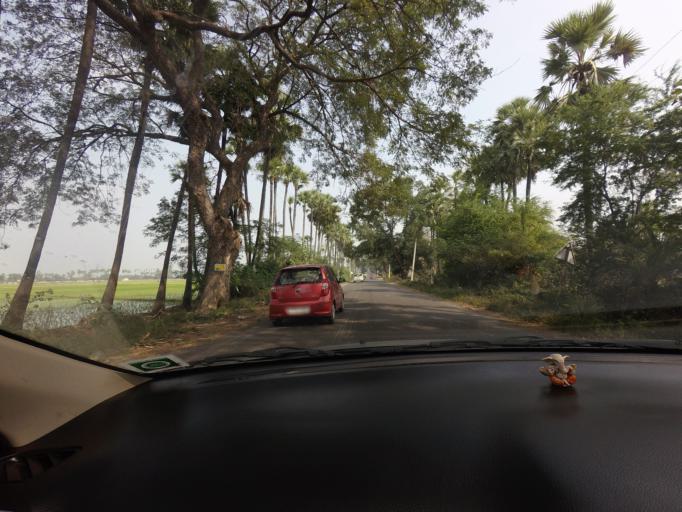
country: IN
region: Andhra Pradesh
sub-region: Krishna
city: Kankipadu
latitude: 16.4540
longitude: 80.7879
